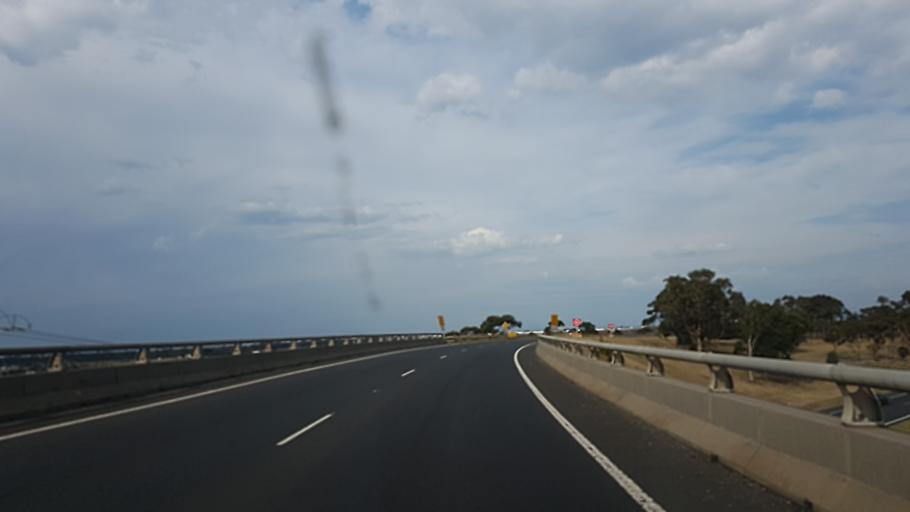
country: AU
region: Victoria
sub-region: Brimbank
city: Keilor Lodge
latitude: -37.7011
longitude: 144.8099
